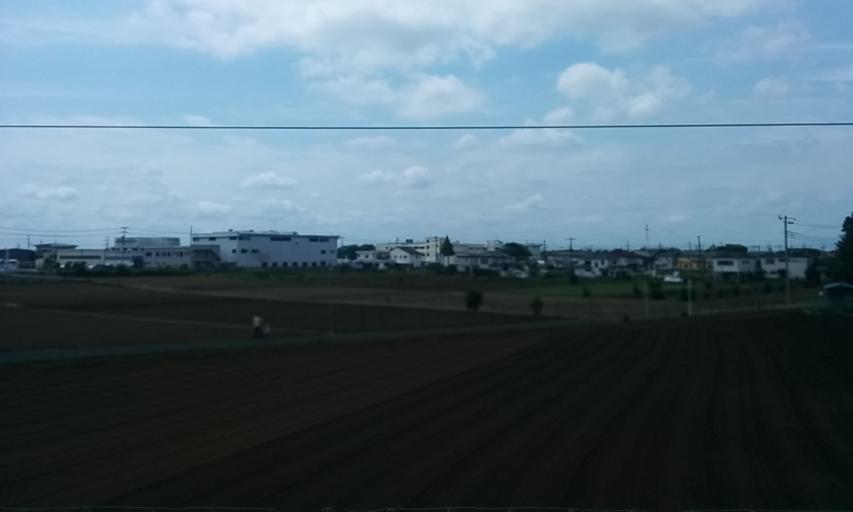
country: JP
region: Chiba
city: Funabashi
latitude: 35.6877
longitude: 140.0732
